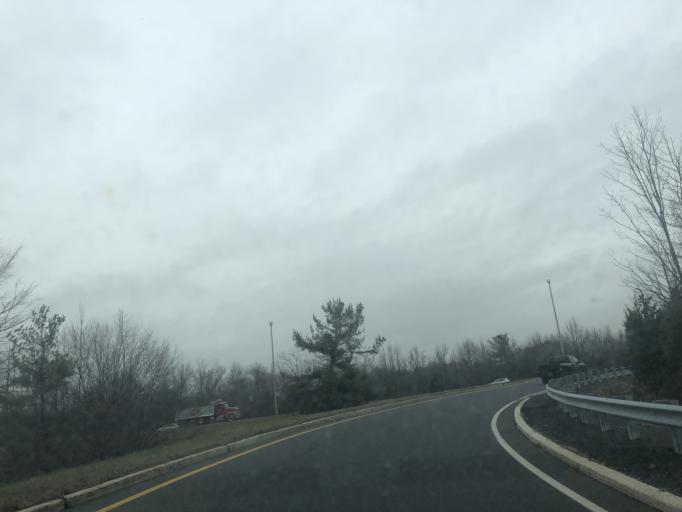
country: US
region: New Jersey
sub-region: Mercer County
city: Robbinsville
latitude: 40.2018
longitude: -74.6378
